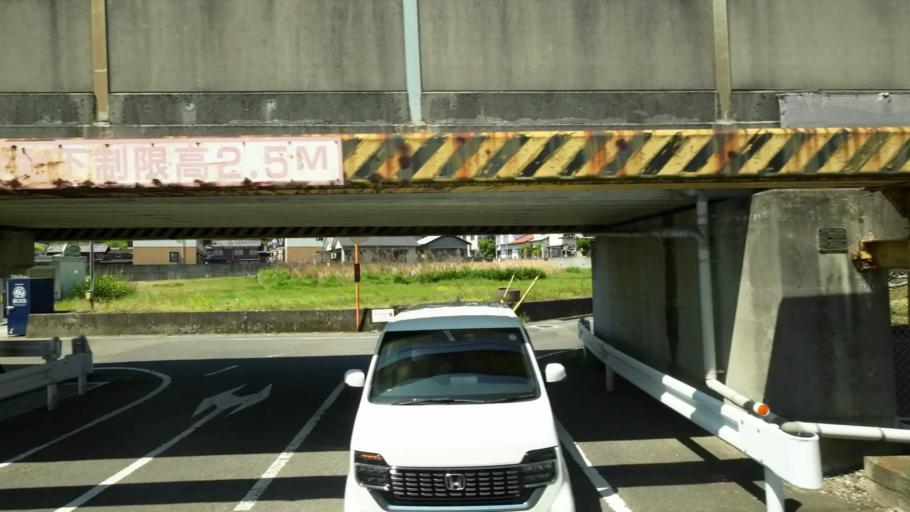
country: JP
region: Ehime
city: Hojo
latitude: 34.0723
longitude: 132.9867
